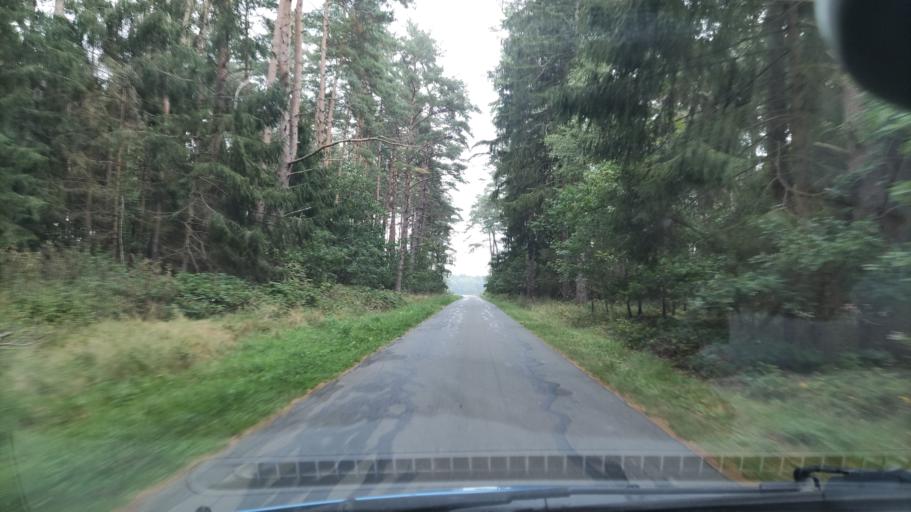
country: DE
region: Lower Saxony
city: Altenmedingen
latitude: 53.1537
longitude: 10.5647
